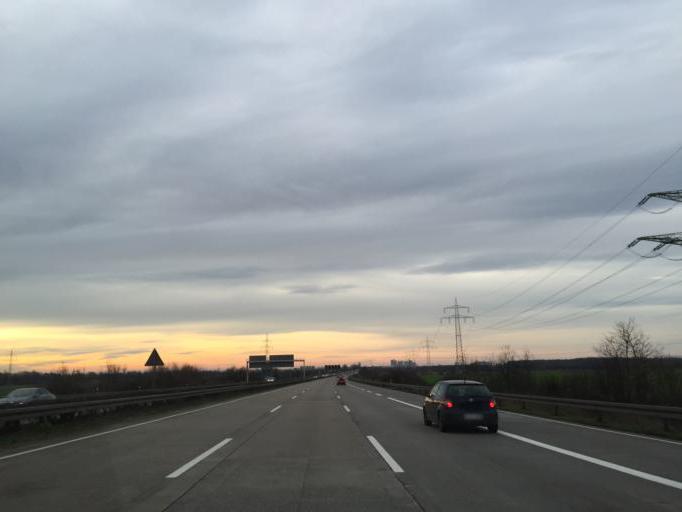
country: DE
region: Lower Saxony
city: Lehrte
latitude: 52.3910
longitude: 9.8996
